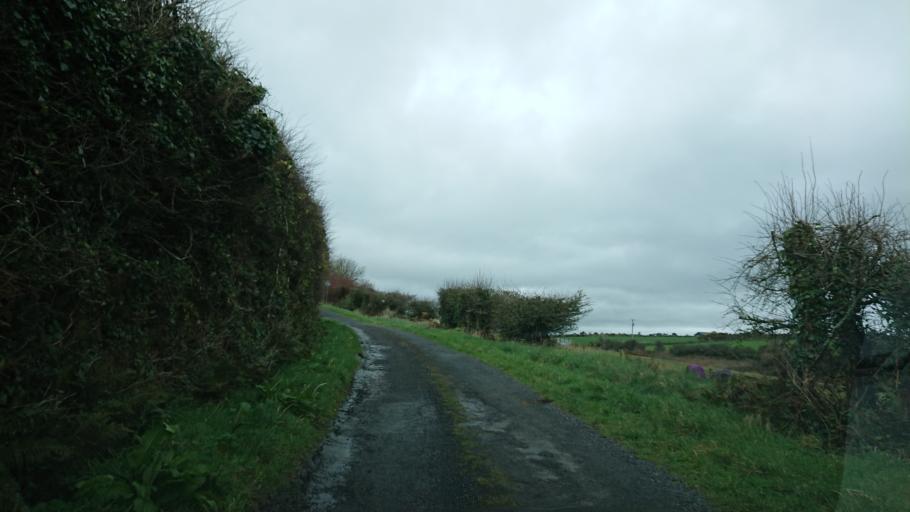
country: IE
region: Munster
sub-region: Waterford
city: Dunmore East
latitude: 52.1431
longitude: -7.0400
